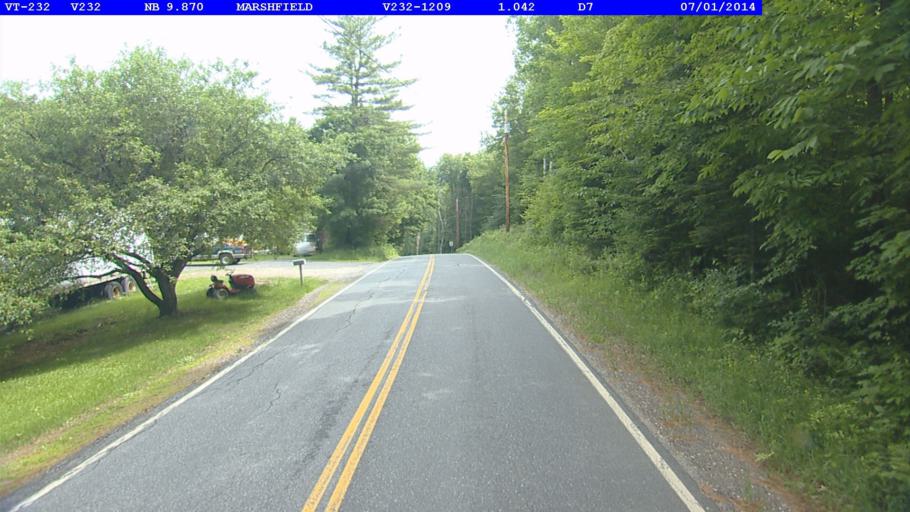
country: US
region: Vermont
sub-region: Caledonia County
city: Hardwick
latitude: 44.3291
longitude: -72.2841
